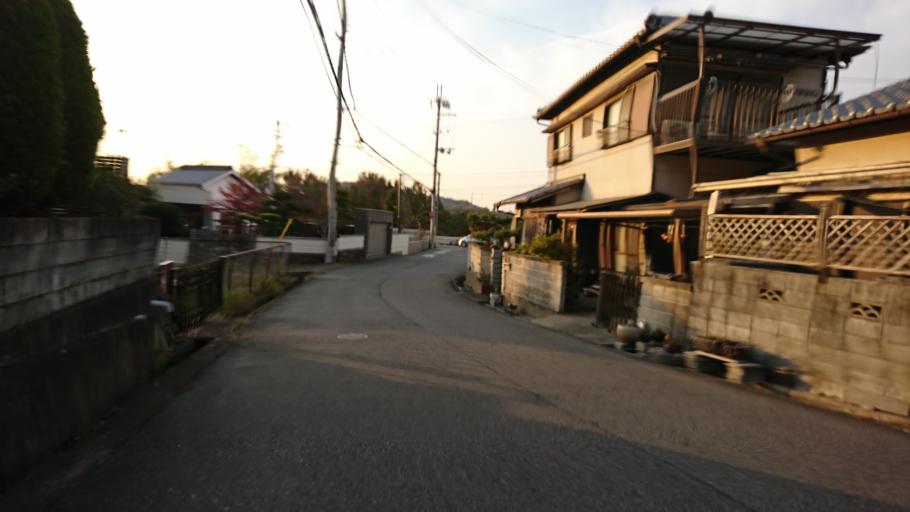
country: JP
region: Hyogo
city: Kakogawacho-honmachi
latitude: 34.7845
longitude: 134.8660
